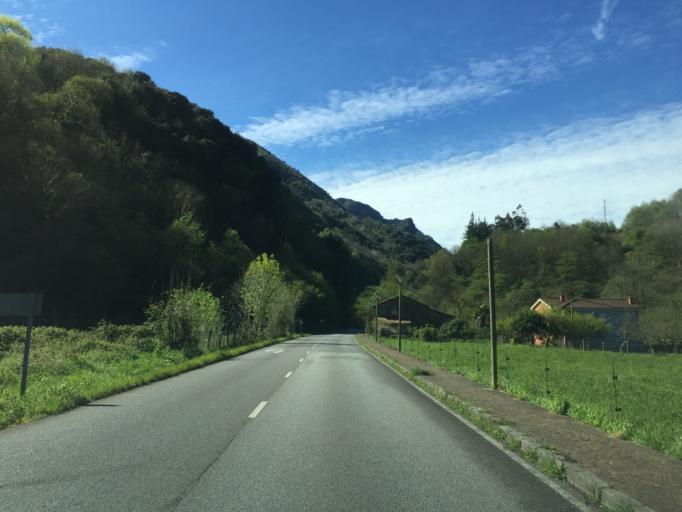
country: ES
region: Asturias
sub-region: Province of Asturias
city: Proaza
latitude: 43.2892
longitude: -5.9829
